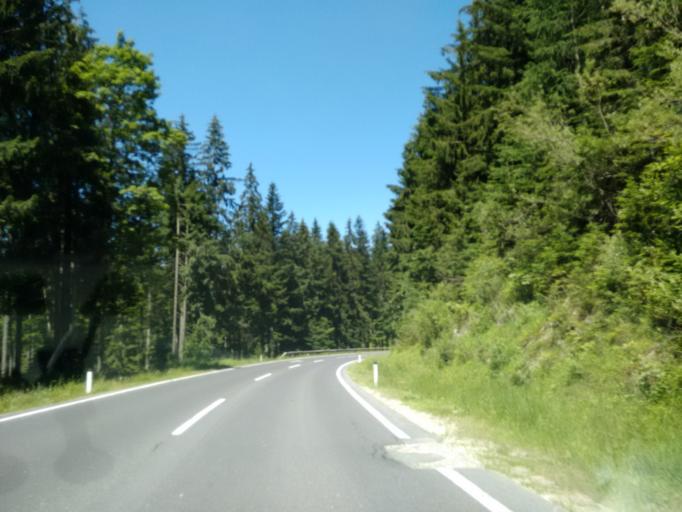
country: AT
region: Styria
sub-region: Politischer Bezirk Liezen
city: Altaussee
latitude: 47.6272
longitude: 13.6914
